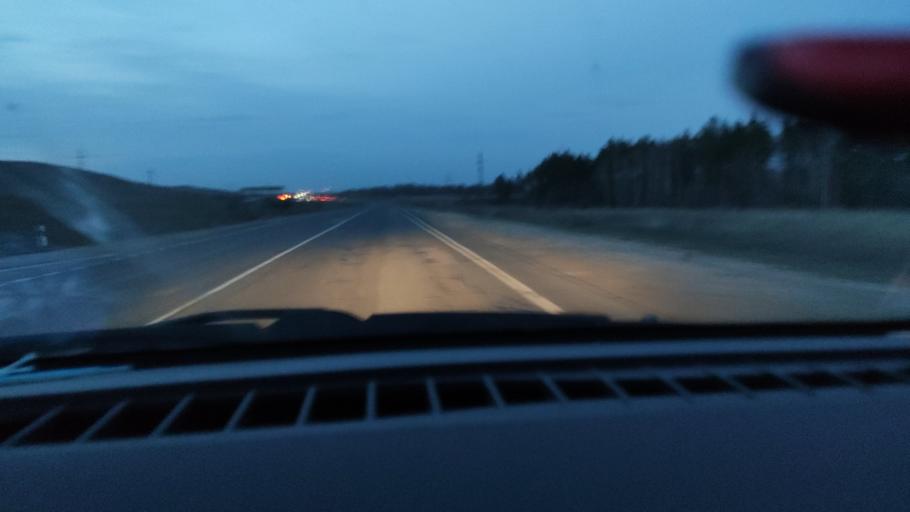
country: RU
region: Saratov
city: Sinodskoye
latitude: 52.0797
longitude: 46.7938
